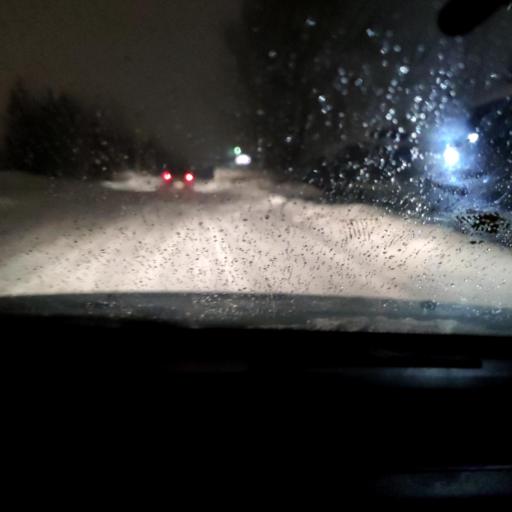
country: RU
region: Perm
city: Kondratovo
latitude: 58.0194
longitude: 56.1333
